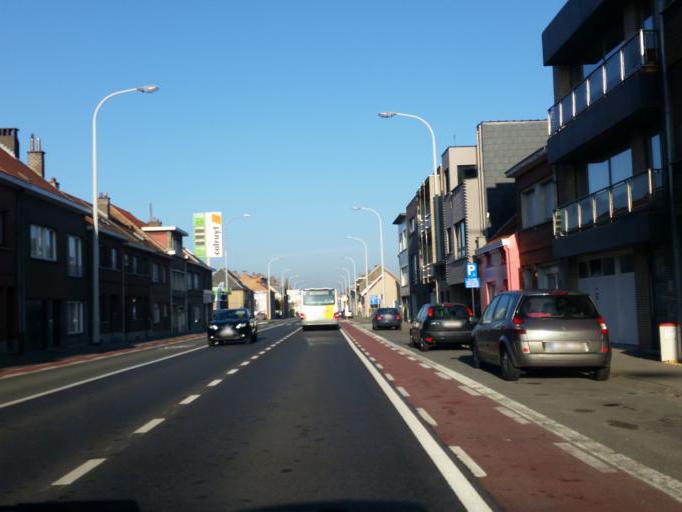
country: BE
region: Flanders
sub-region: Provincie Vlaams-Brabant
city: Asse
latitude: 50.9161
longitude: 4.1907
